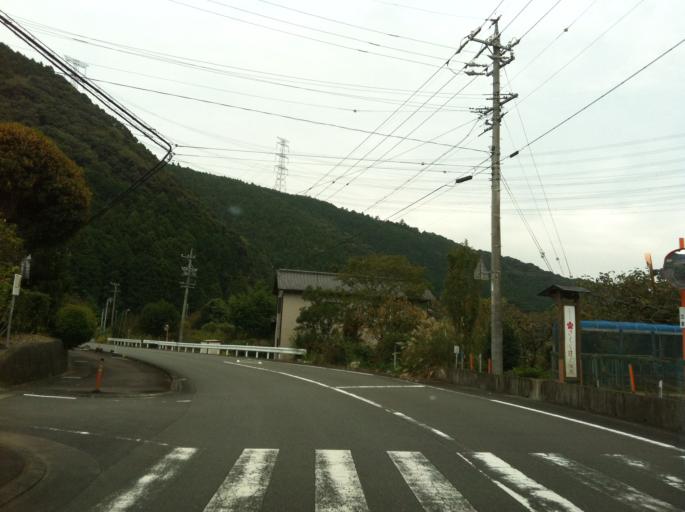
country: JP
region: Shizuoka
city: Mori
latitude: 34.8650
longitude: 138.0180
